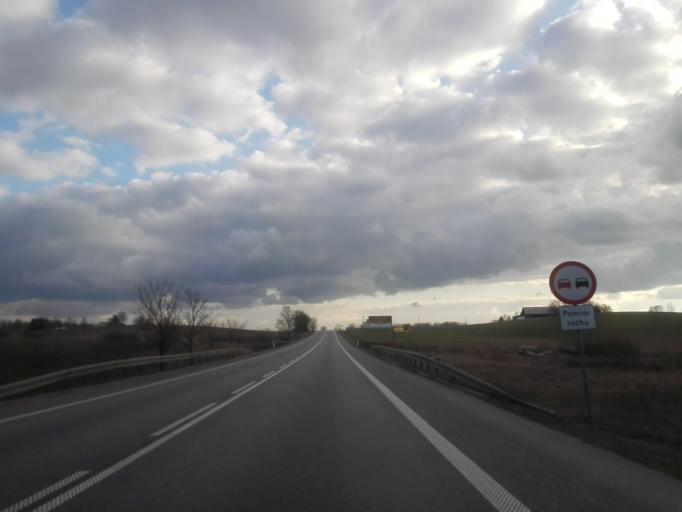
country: PL
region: Podlasie
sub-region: Suwalki
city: Suwalki
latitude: 54.2053
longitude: 23.0239
